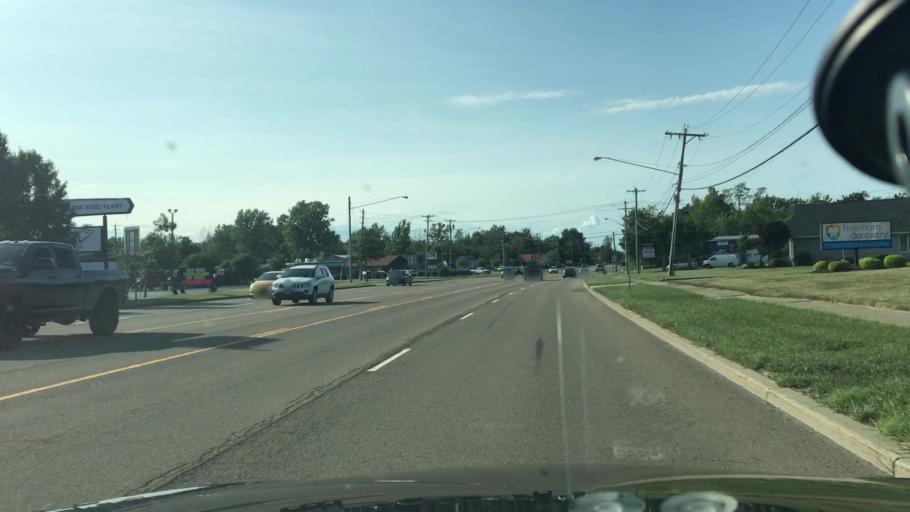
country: US
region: New York
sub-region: Erie County
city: Wanakah
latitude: 42.7572
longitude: -78.8602
